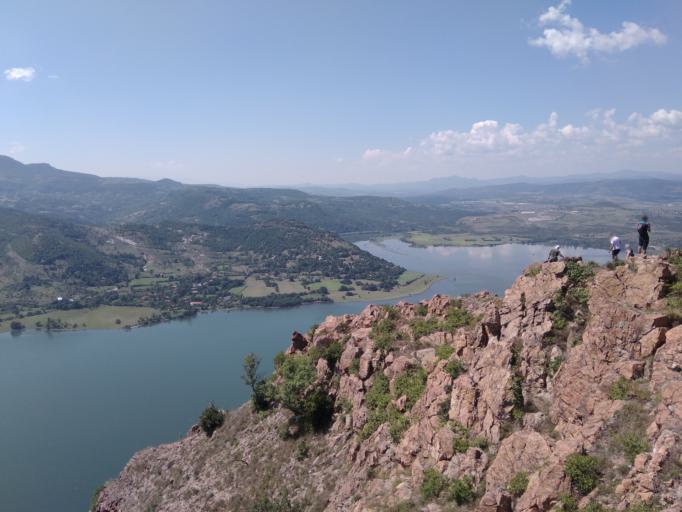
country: BG
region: Kurdzhali
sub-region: Obshtina Kurdzhali
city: Kurdzhali
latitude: 41.6232
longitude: 25.4579
